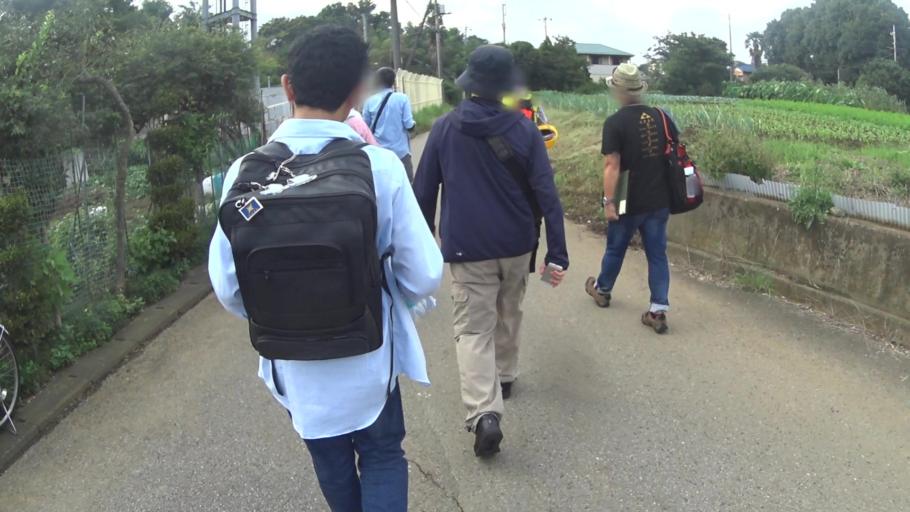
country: JP
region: Saitama
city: Kasukabe
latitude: 35.9650
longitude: 139.7165
